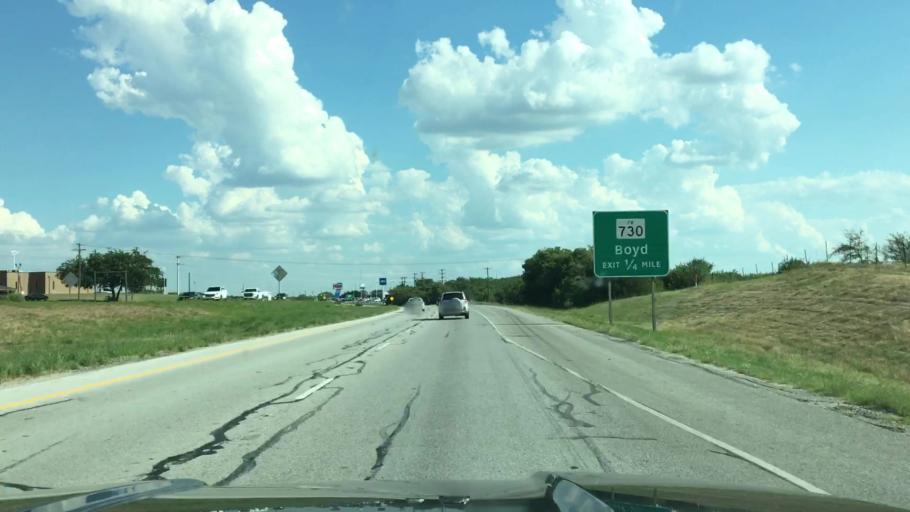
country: US
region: Texas
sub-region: Wise County
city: Decatur
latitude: 33.2196
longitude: -97.5889
